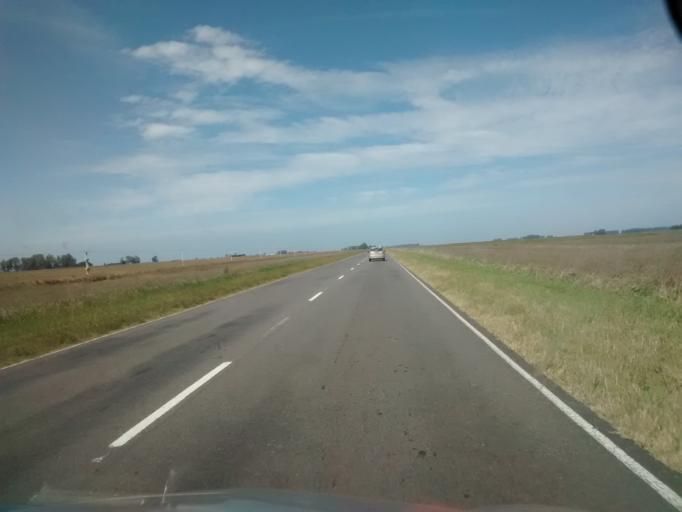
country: AR
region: Buenos Aires
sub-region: Partido de Ayacucho
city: Ayacucho
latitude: -36.6678
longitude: -58.5745
